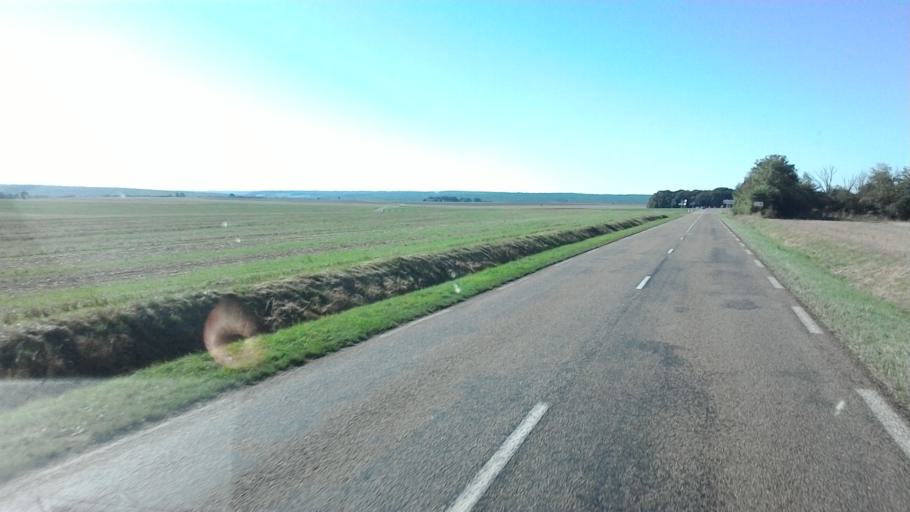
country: FR
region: Champagne-Ardenne
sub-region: Departement de la Haute-Marne
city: Chateauvillain
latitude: 47.9486
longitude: 4.8735
